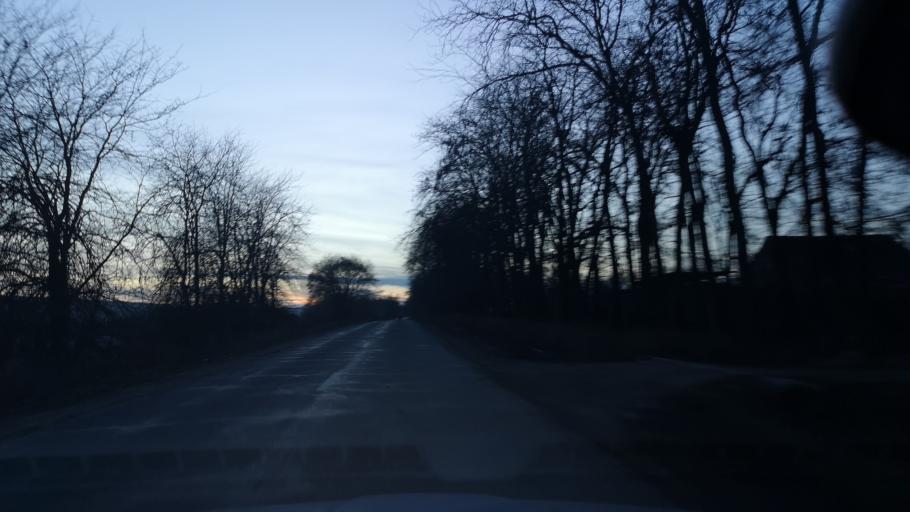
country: MD
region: Orhei
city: Orhei
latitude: 47.2951
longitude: 28.8997
